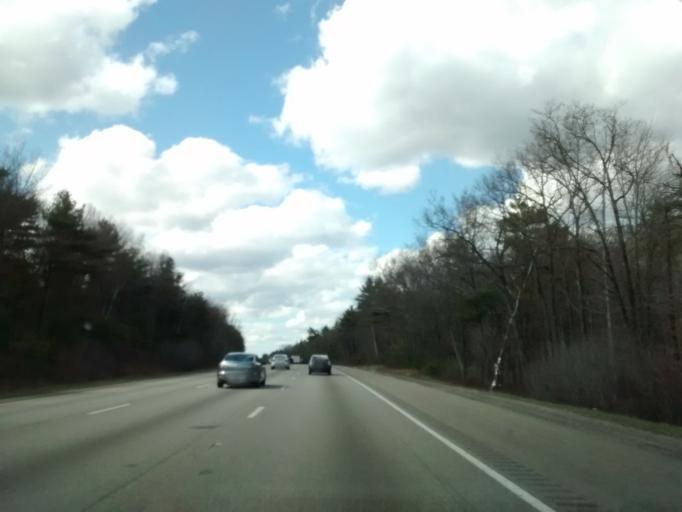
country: US
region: Massachusetts
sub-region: Middlesex County
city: Hopkinton
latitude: 42.2354
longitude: -71.5510
